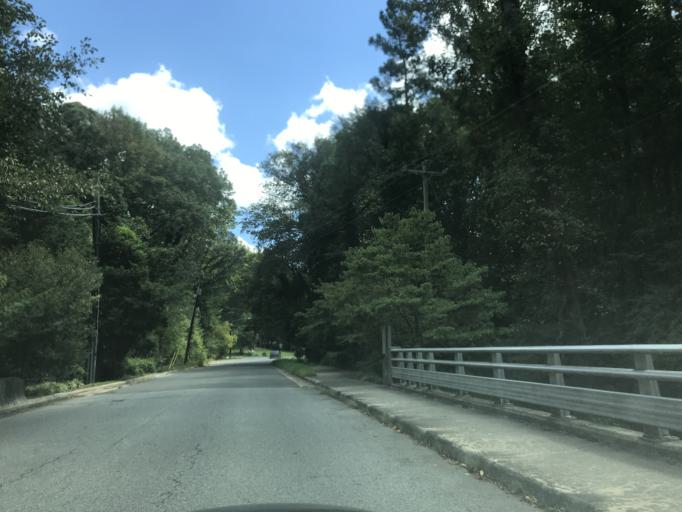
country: US
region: North Carolina
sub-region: Orange County
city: Chapel Hill
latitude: 35.9301
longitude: -79.0215
